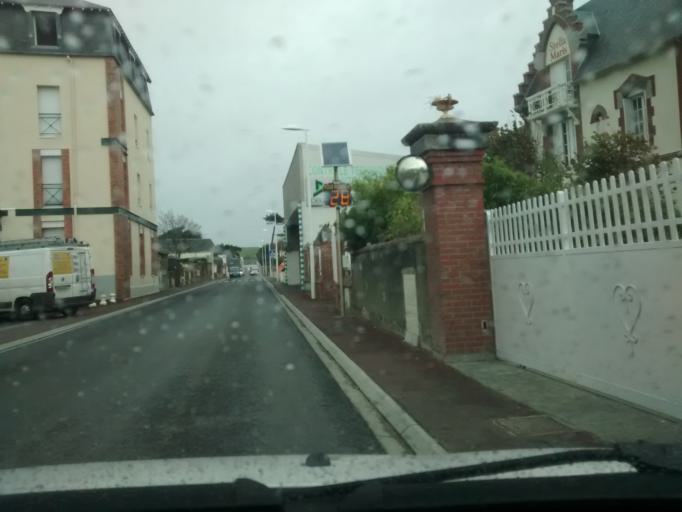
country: FR
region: Lower Normandy
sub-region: Departement de la Manche
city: Saint-Pair-sur-Mer
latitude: 48.8173
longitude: -1.5720
